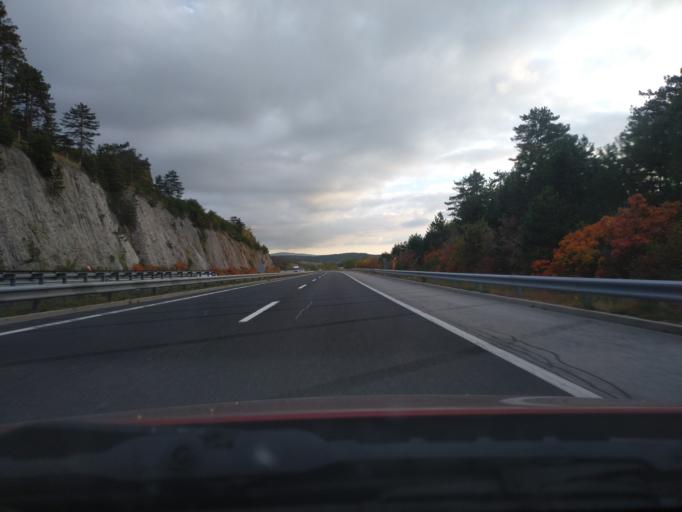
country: SI
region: Hrpelje-Kozina
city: Kozina
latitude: 45.5965
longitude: 13.9297
